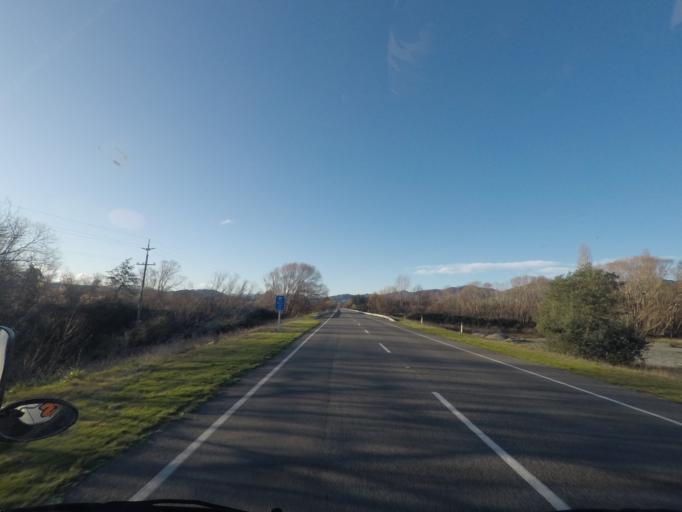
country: NZ
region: Canterbury
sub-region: Kaikoura District
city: Kaikoura
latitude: -42.7247
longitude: 173.2814
